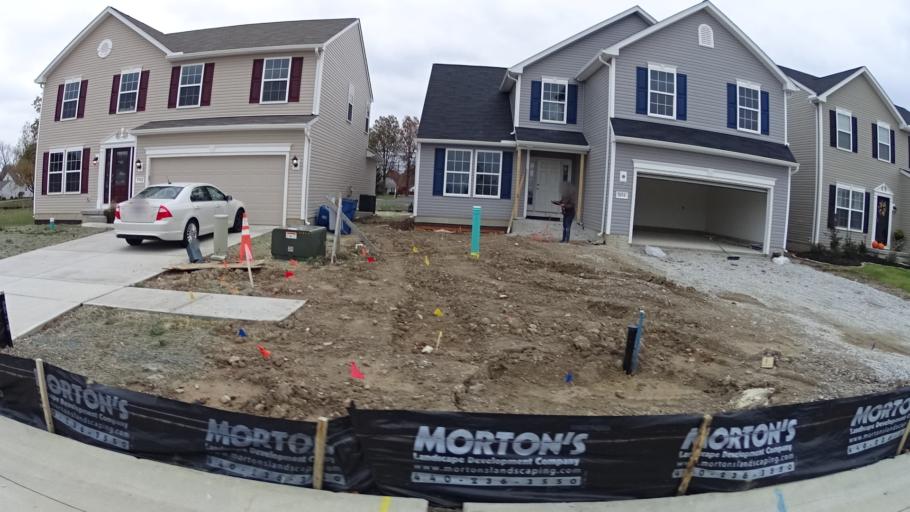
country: US
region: Ohio
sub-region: Lorain County
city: Lorain
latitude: 41.4408
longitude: -82.2159
